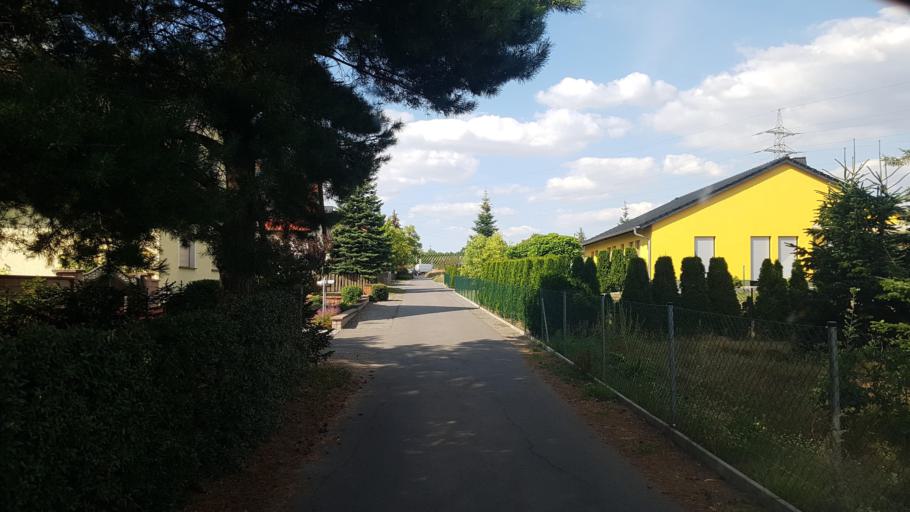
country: DE
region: Saxony-Anhalt
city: Jessen
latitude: 51.7952
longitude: 12.9747
